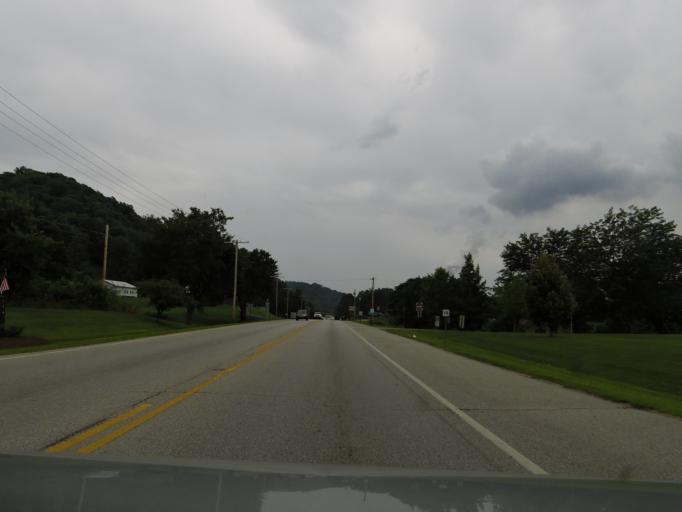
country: US
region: Ohio
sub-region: Brown County
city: Ripley
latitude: 38.7251
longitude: -83.8308
